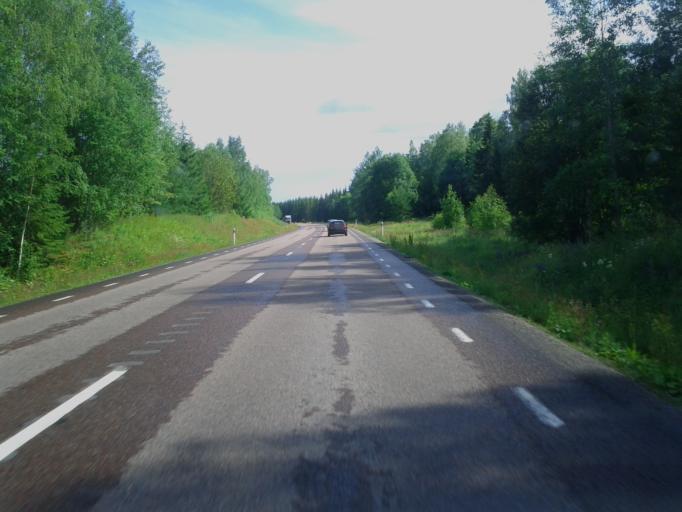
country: SE
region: Dalarna
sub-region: Faluns Kommun
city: Falun
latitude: 60.6555
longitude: 15.5550
